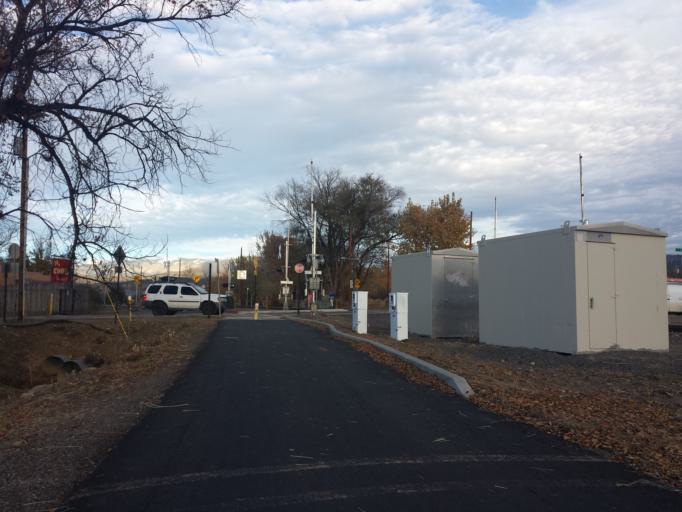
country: US
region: New Mexico
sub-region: Santa Fe County
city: Santa Fe
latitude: 35.6786
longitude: -105.9532
